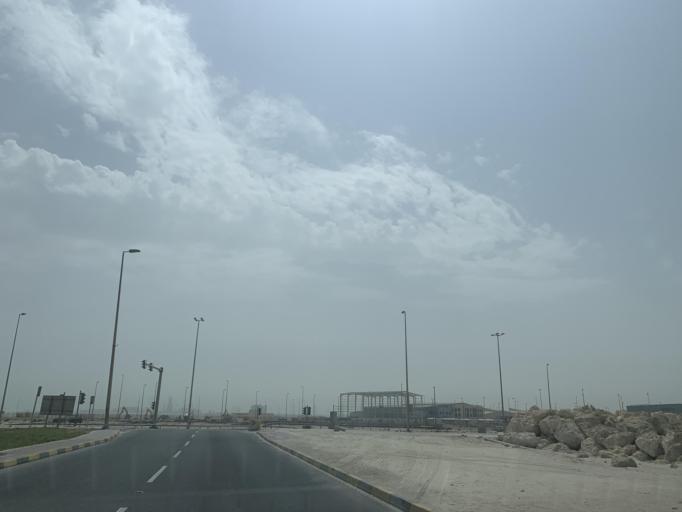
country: BH
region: Muharraq
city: Al Hadd
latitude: 26.2250
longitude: 50.6964
